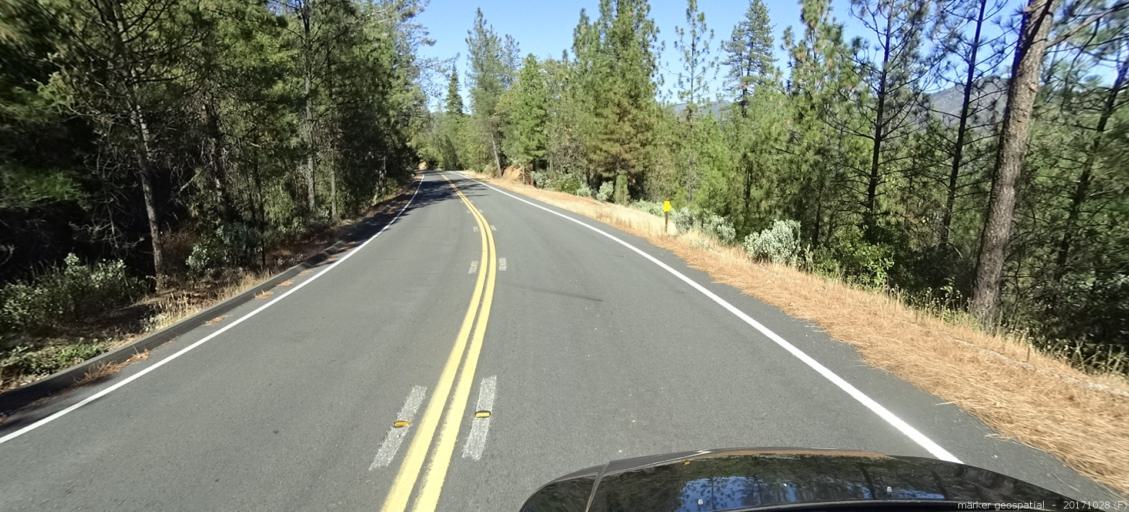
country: US
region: California
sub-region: Shasta County
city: Shasta
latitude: 40.6139
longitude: -122.5652
